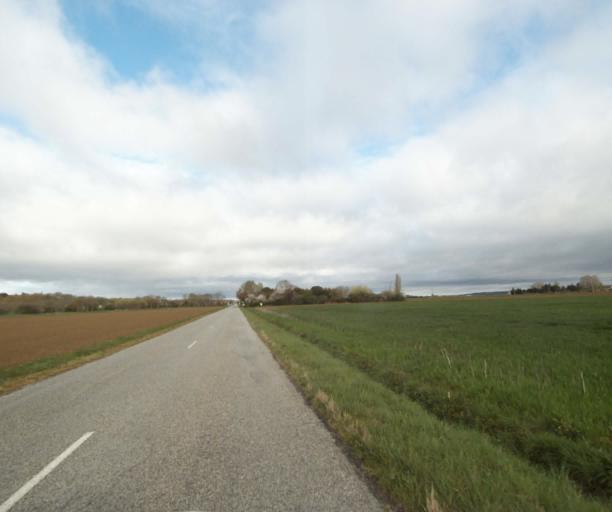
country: FR
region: Midi-Pyrenees
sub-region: Departement de l'Ariege
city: Saverdun
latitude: 43.2543
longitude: 1.5432
